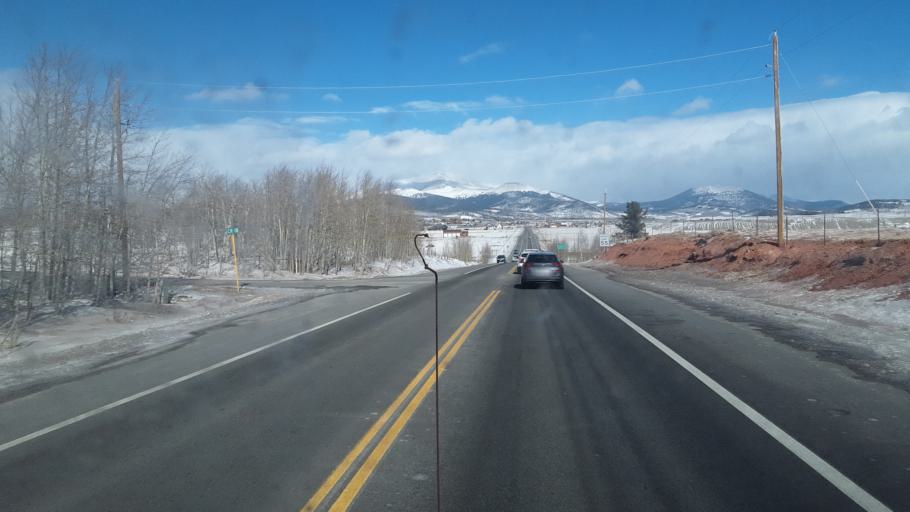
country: US
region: Colorado
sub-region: Park County
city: Fairplay
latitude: 39.2029
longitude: -105.9952
